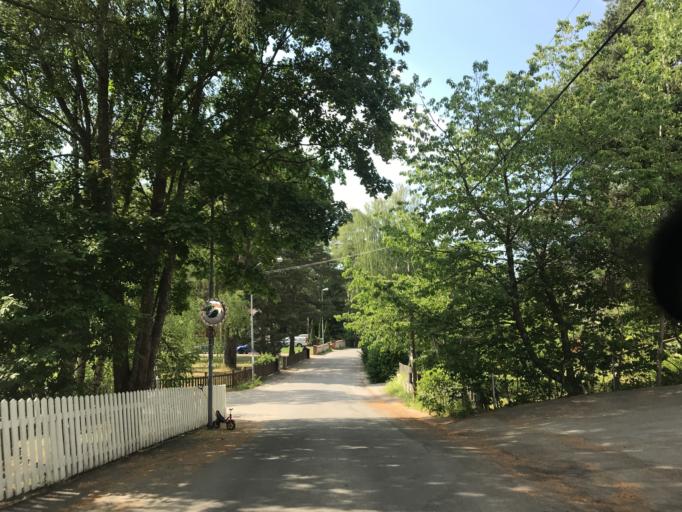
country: SE
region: Stockholm
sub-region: Stockholms Kommun
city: Kista
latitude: 59.4089
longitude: 17.9700
